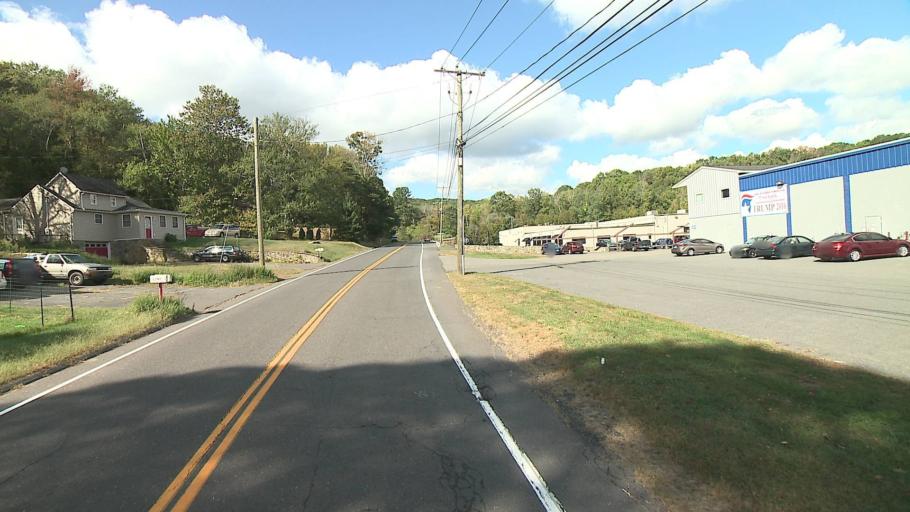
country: US
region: Connecticut
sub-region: New Haven County
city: Seymour
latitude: 41.4275
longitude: -73.0806
